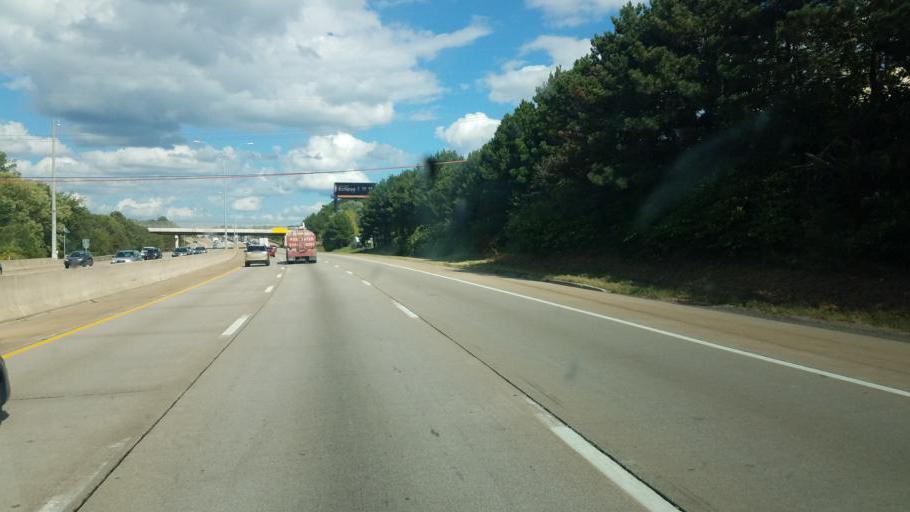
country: US
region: Ohio
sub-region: Summit County
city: Sawyerwood
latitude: 41.0641
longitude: -81.4434
